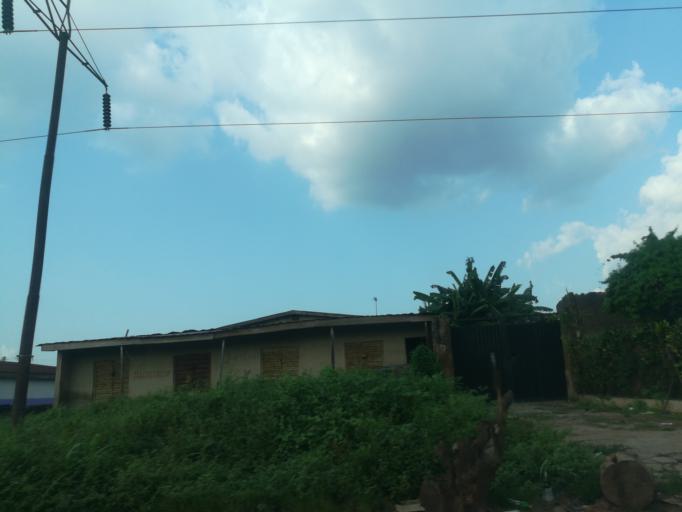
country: NG
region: Oyo
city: Moniya
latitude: 7.4794
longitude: 3.9100
